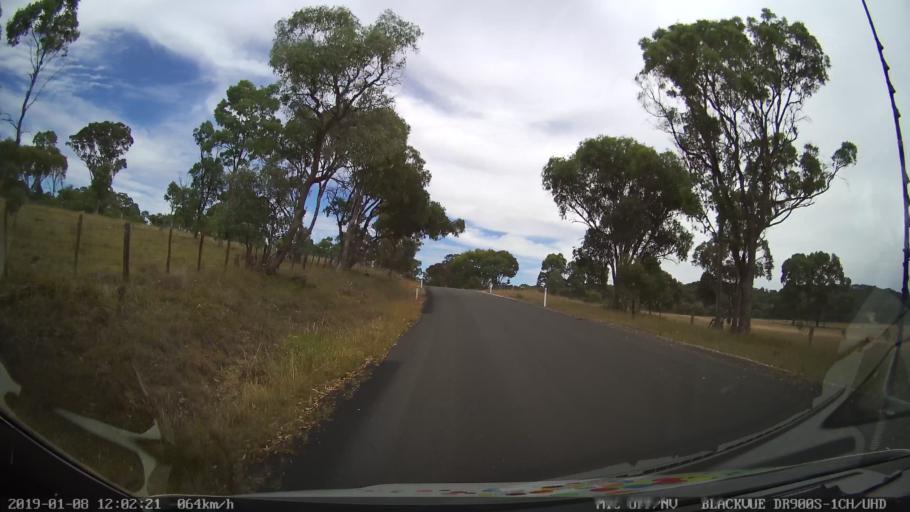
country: AU
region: New South Wales
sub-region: Armidale Dumaresq
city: Armidale
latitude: -30.4548
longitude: 151.6046
